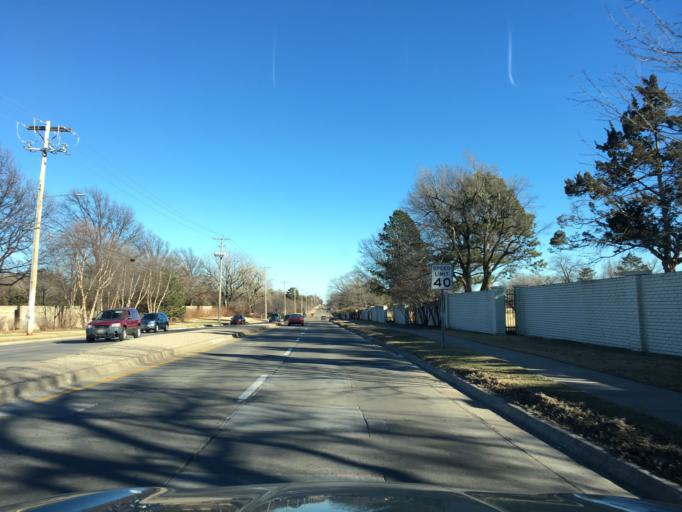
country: US
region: Kansas
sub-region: Sedgwick County
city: Bellaire
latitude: 37.7084
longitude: -97.2442
